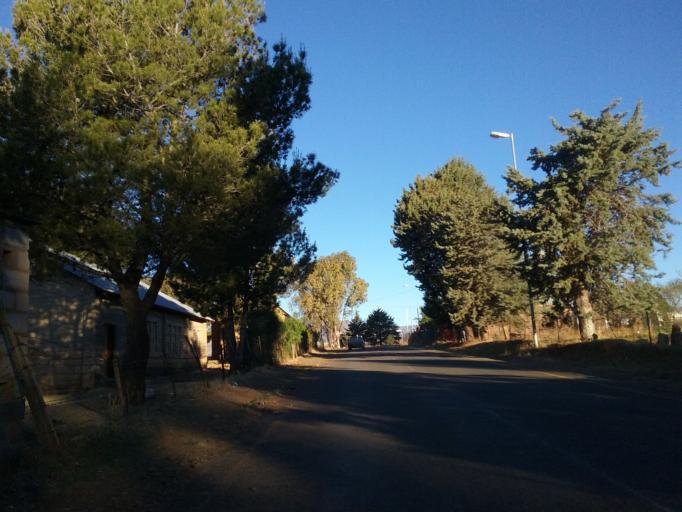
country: LS
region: Quthing
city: Quthing
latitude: -30.4054
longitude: 27.7070
